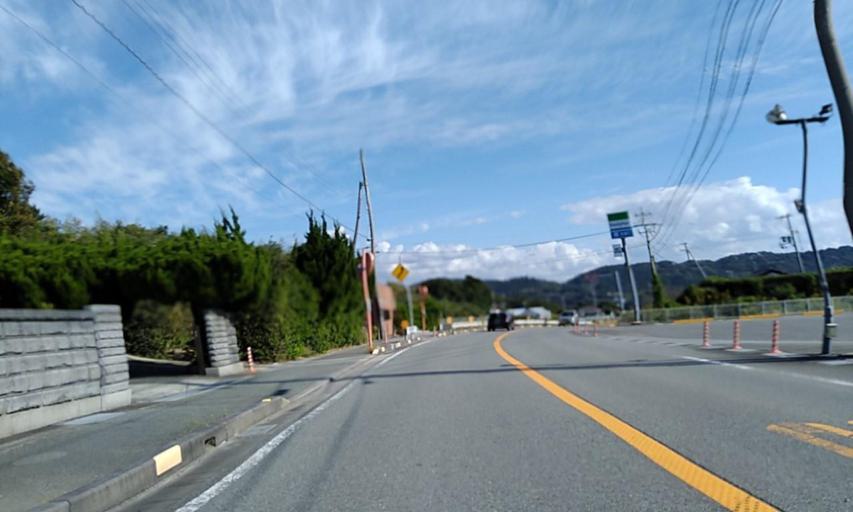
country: JP
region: Wakayama
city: Gobo
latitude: 33.8037
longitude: 135.2269
